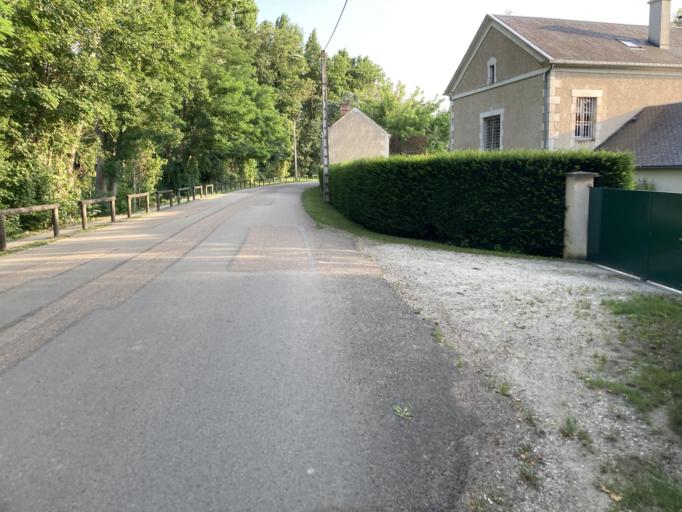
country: FR
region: Bourgogne
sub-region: Departement de l'Yonne
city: Saint-Bris-le-Vineux
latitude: 47.7072
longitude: 3.6373
